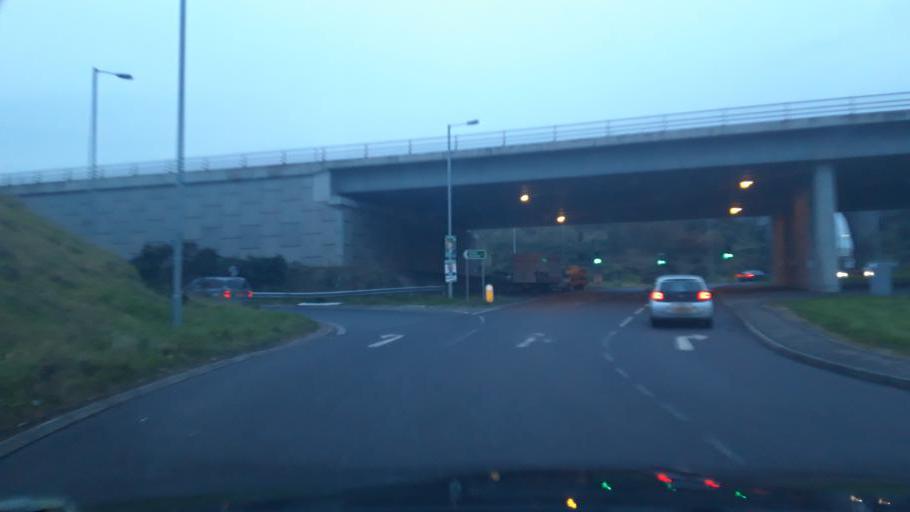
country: GB
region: Northern Ireland
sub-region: Newry and Mourne District
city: Newry
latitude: 54.1855
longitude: -6.3600
